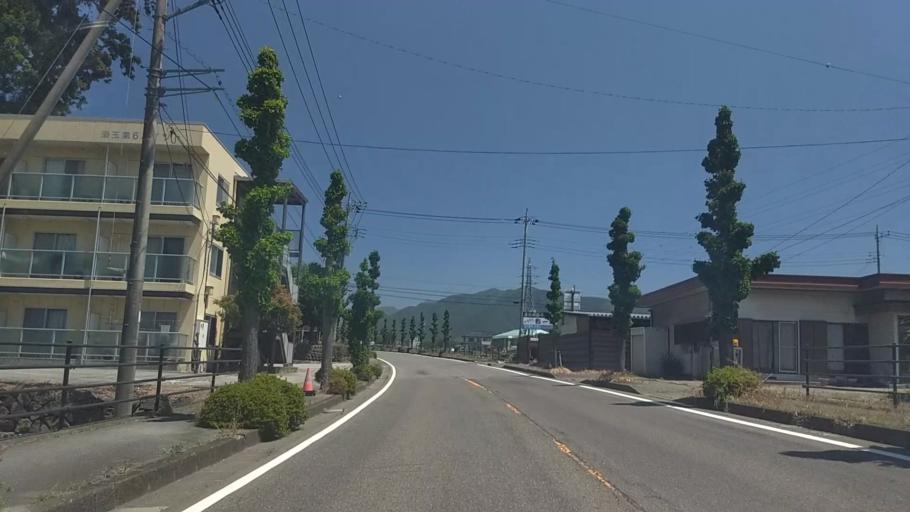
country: JP
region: Yamanashi
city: Nirasaki
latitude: 35.7968
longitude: 138.4239
